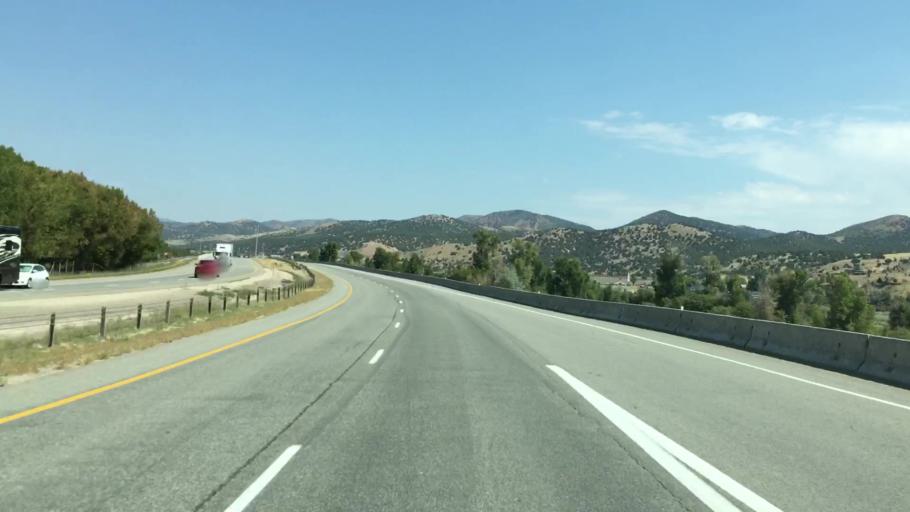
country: US
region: Utah
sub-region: Summit County
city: Coalville
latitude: 40.8104
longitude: -111.4032
